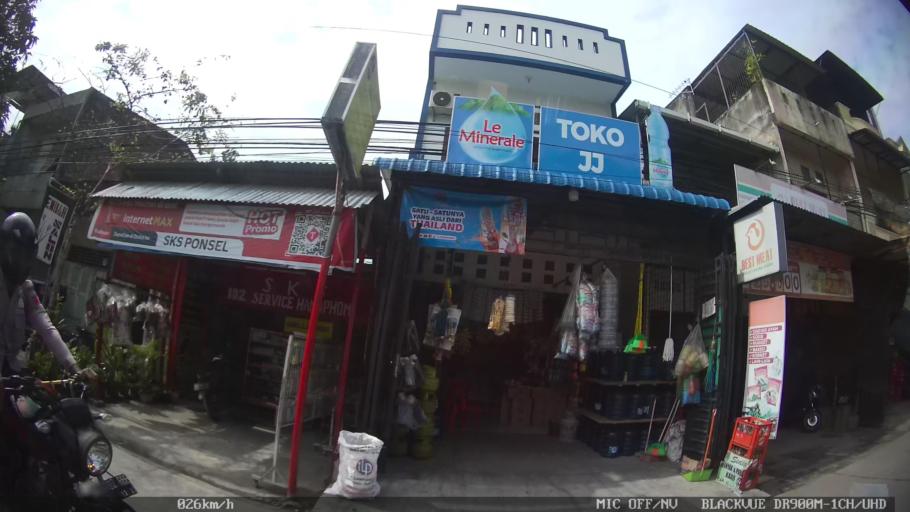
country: ID
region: North Sumatra
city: Sunggal
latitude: 3.6062
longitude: 98.6143
